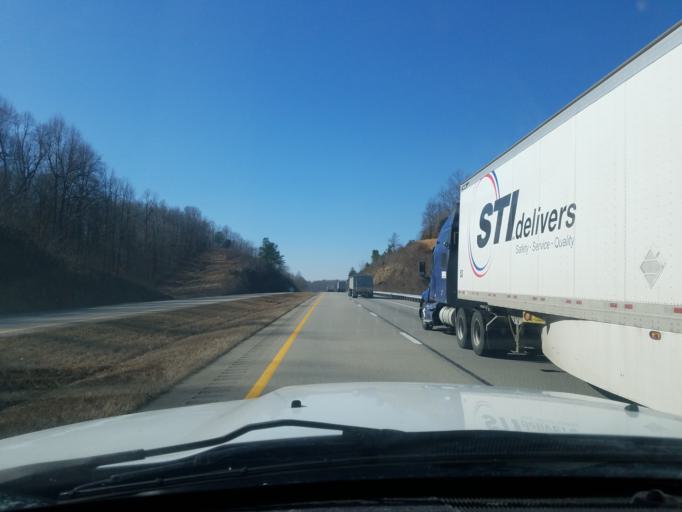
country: US
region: Kentucky
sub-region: Ohio County
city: Oak Grove
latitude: 37.3880
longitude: -86.6850
